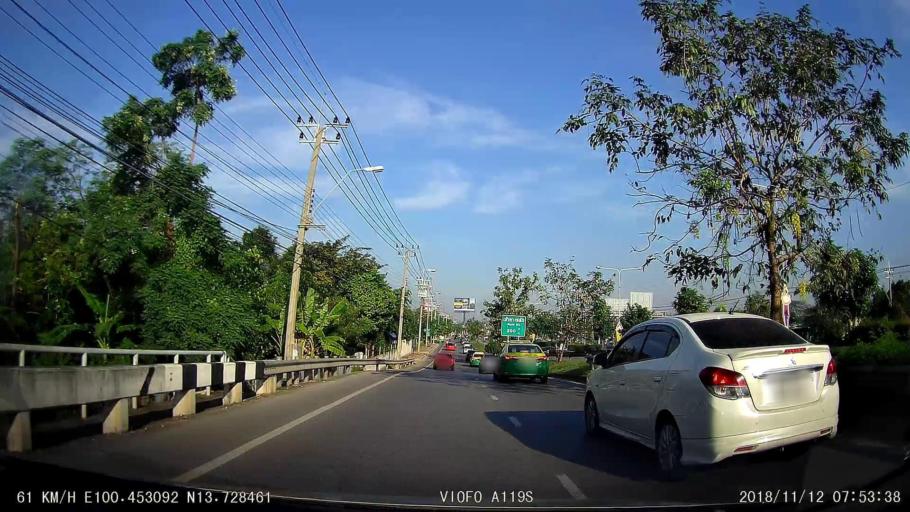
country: TH
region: Bangkok
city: Phasi Charoen
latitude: 13.7286
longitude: 100.4530
